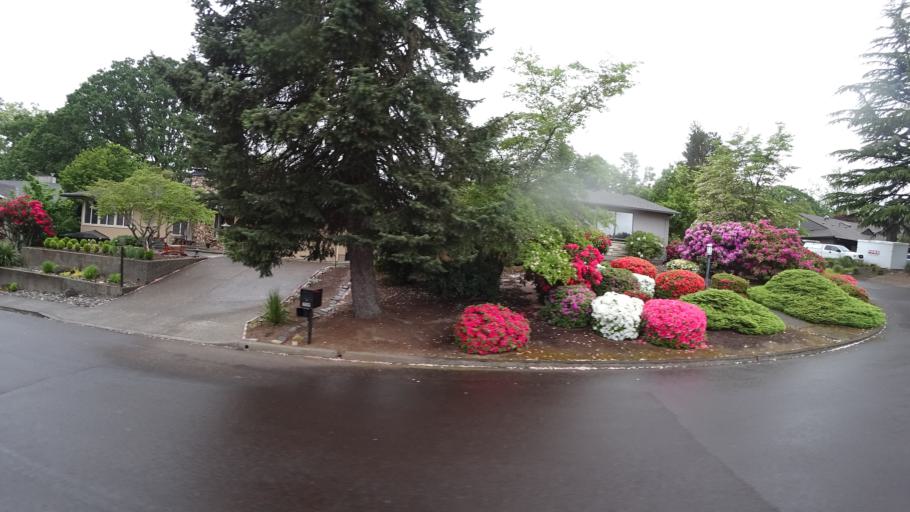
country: US
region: Oregon
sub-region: Washington County
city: Raleigh Hills
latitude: 45.4738
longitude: -122.7690
